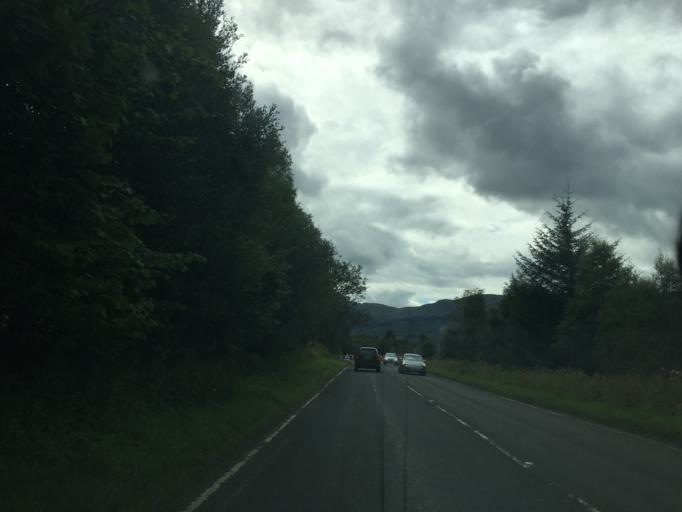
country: GB
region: Scotland
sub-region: Stirling
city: Callander
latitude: 56.3330
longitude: -4.3242
